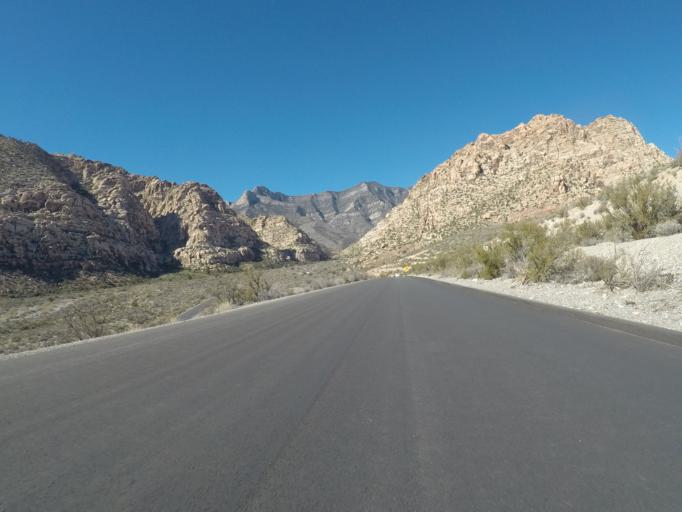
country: US
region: Nevada
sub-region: Clark County
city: Summerlin South
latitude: 36.1546
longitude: -115.4871
